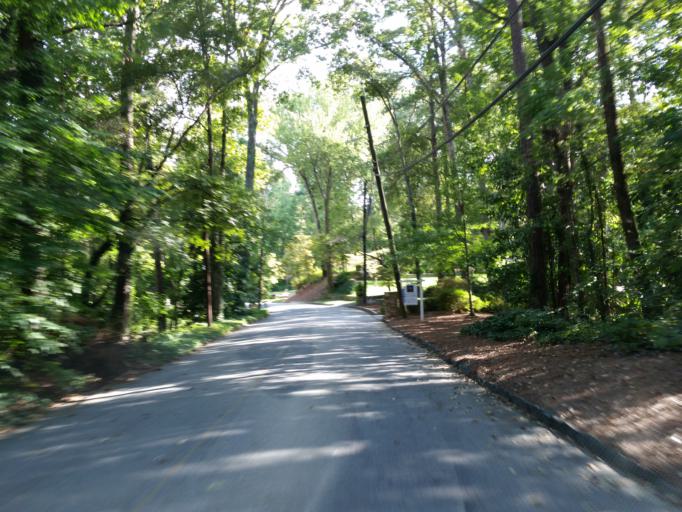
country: US
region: Georgia
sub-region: Cobb County
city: Vinings
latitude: 33.8649
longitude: -84.4348
